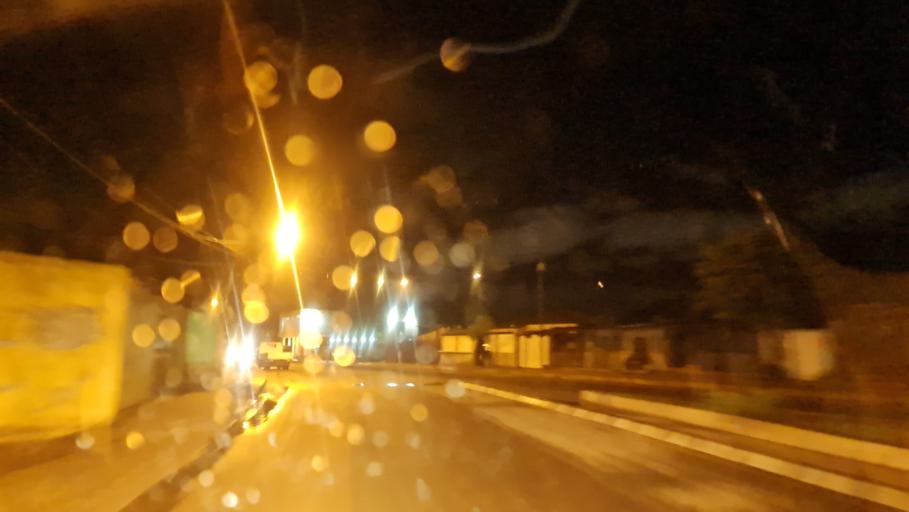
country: MZ
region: Nampula
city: Nampula
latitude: -15.1127
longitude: 39.2836
